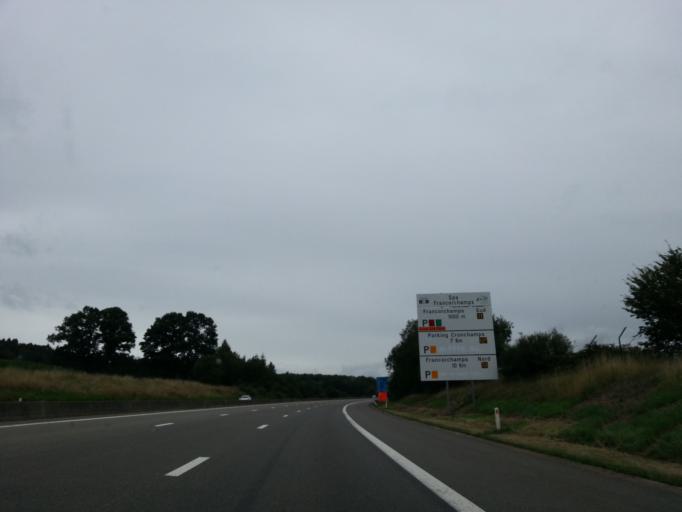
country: BE
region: Wallonia
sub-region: Province de Liege
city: Stavelot
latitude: 50.3949
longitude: 5.9831
